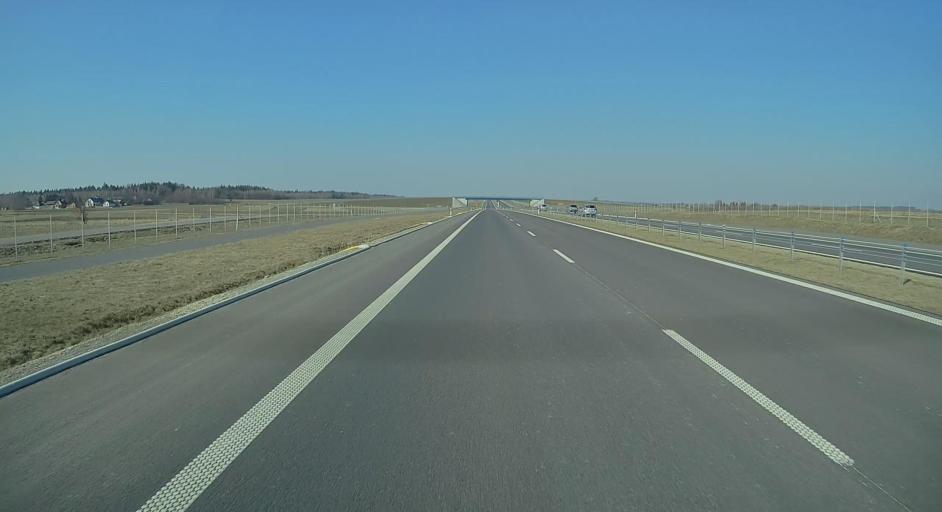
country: PL
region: Lublin Voivodeship
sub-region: Powiat janowski
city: Modliborzyce
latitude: 50.7400
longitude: 22.3228
